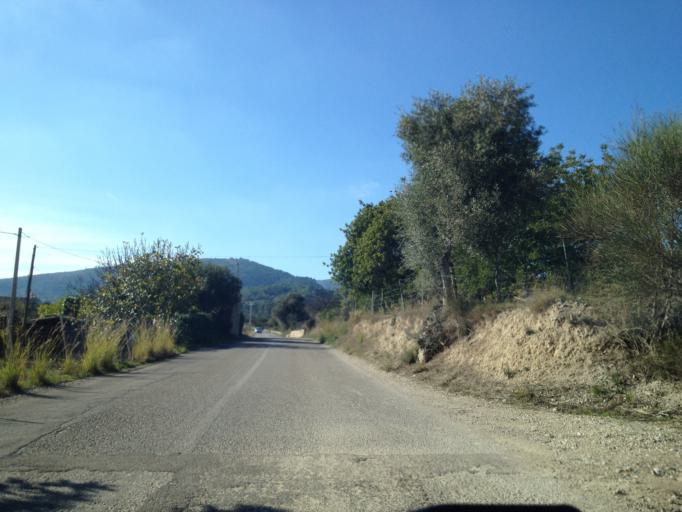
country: ES
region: Balearic Islands
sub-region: Illes Balears
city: Selva
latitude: 39.7417
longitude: 2.8946
